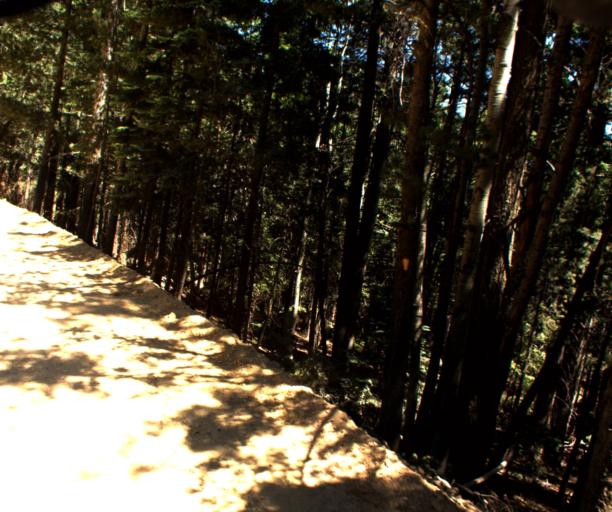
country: US
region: Arizona
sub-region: Graham County
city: Swift Trail Junction
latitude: 32.6642
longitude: -109.8718
